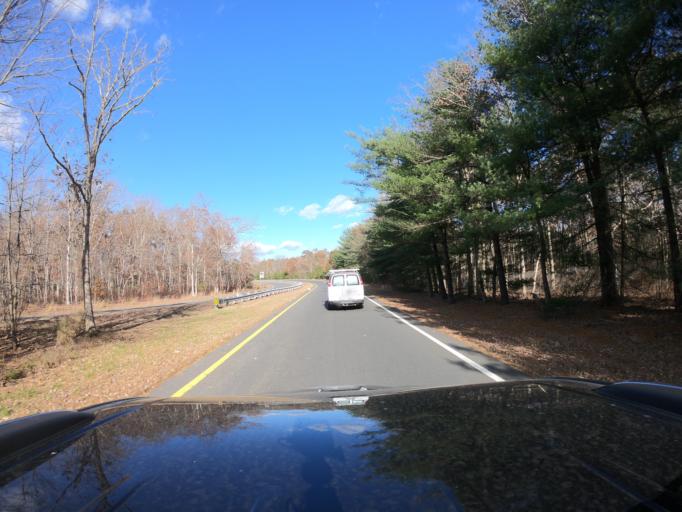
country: US
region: New Jersey
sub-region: Ocean County
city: Lakewood
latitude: 40.1634
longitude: -74.2336
